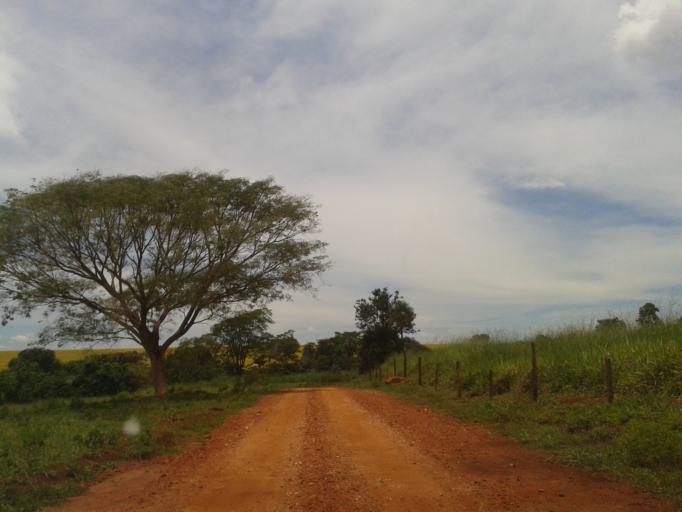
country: BR
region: Minas Gerais
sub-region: Capinopolis
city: Capinopolis
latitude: -18.6827
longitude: -49.7132
